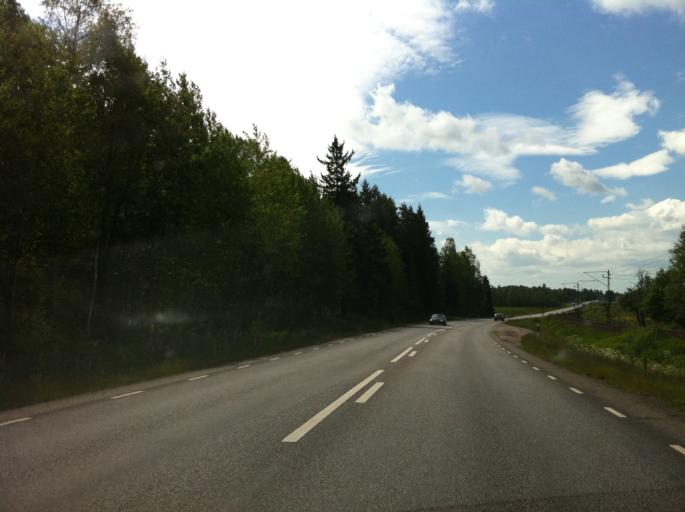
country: SE
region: Vaermland
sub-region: Saffle Kommun
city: Saeffle
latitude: 59.1987
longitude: 13.0245
